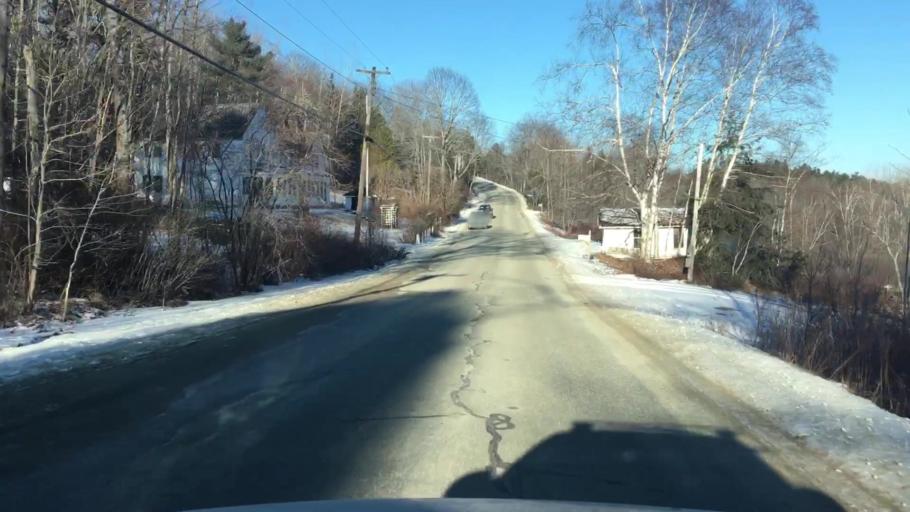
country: US
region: Maine
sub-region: Hancock County
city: Castine
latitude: 44.3502
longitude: -68.7818
